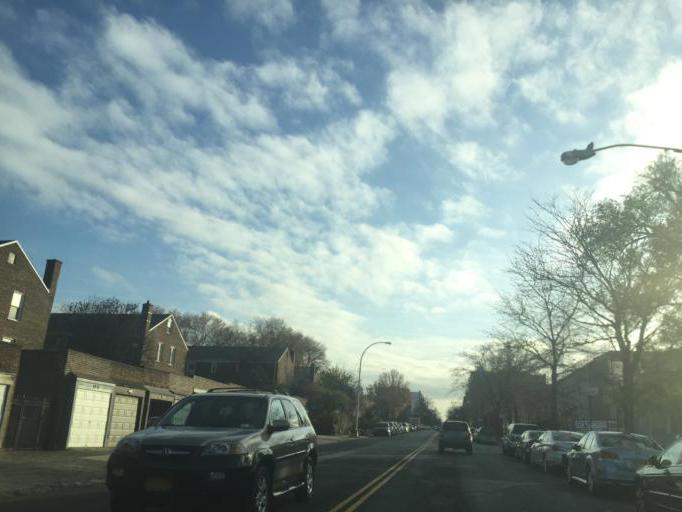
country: US
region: New York
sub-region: Queens County
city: Long Island City
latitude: 40.7488
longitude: -73.9204
